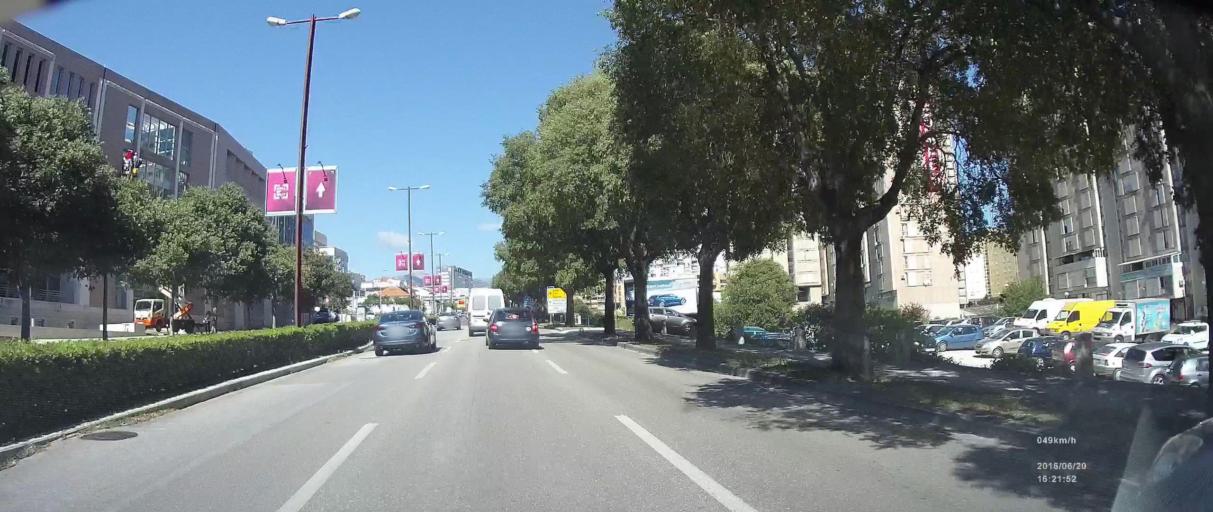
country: HR
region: Splitsko-Dalmatinska
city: Vranjic
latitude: 43.5084
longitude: 16.4732
